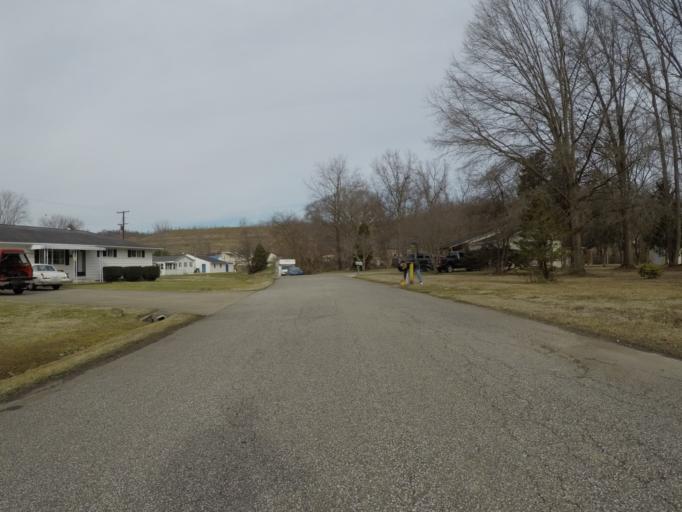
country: US
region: West Virginia
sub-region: Cabell County
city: Pea Ridge
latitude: 38.4462
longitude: -82.3715
